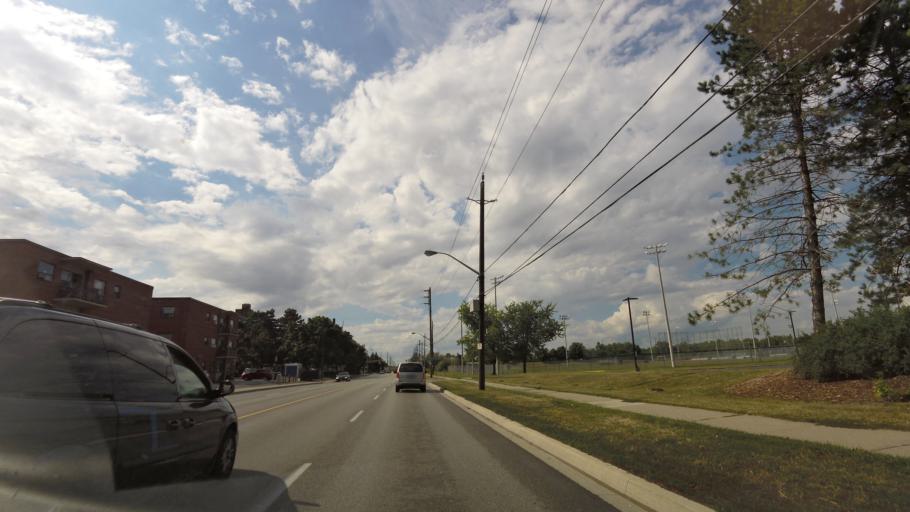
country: CA
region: Ontario
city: Brampton
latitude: 43.6811
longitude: -79.7773
